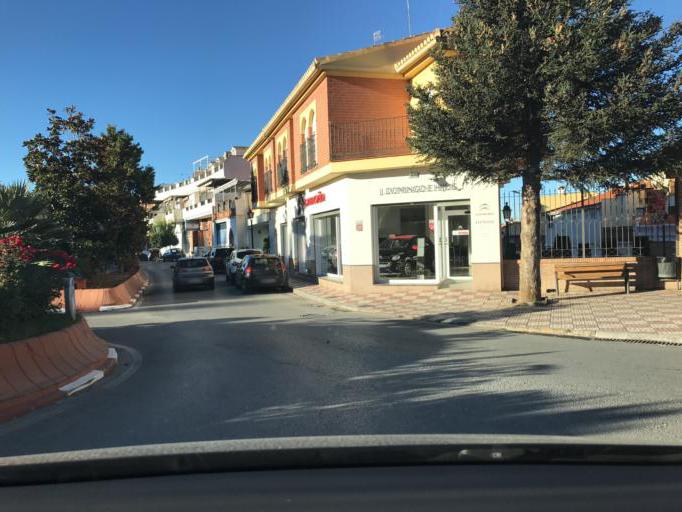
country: ES
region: Andalusia
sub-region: Provincia de Granada
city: Alfacar
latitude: 37.2363
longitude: -3.5652
